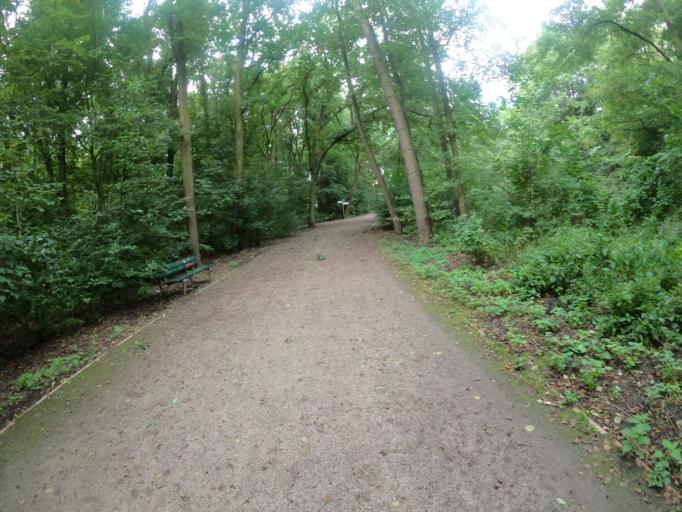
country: DE
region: Berlin
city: Siemensstadt
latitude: 52.5420
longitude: 13.2791
